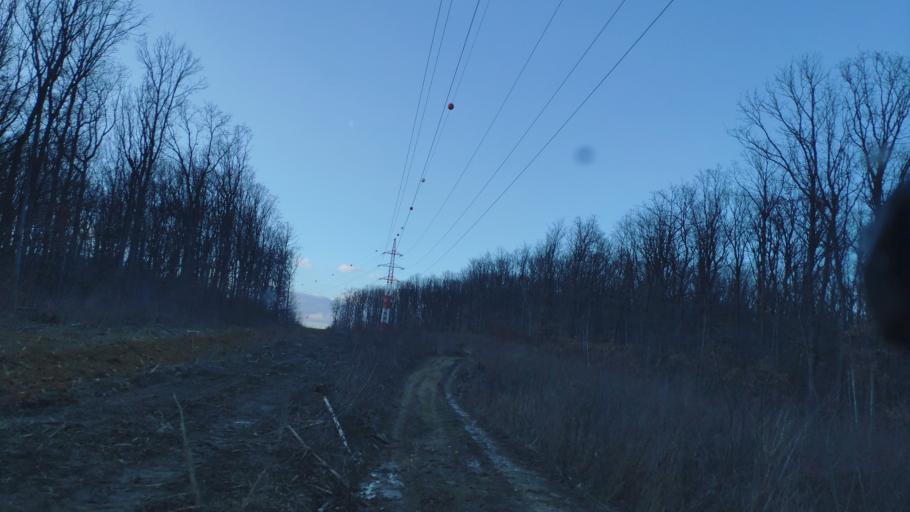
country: SK
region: Kosicky
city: Kosice
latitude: 48.6943
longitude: 21.1813
